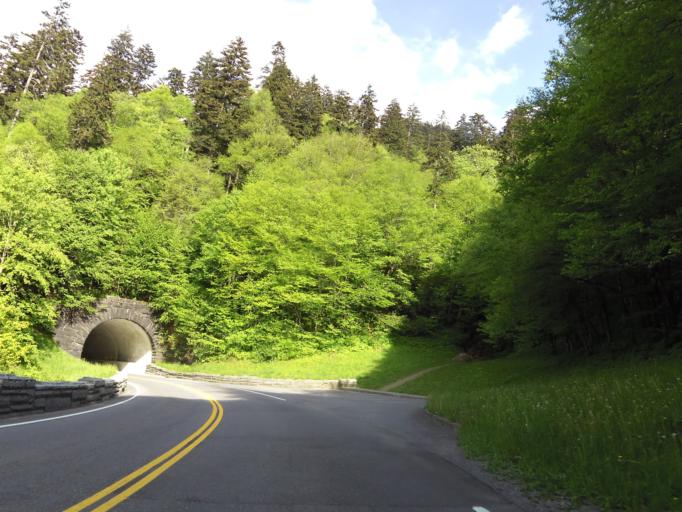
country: US
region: Tennessee
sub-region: Sevier County
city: Gatlinburg
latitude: 35.6168
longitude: -83.4206
